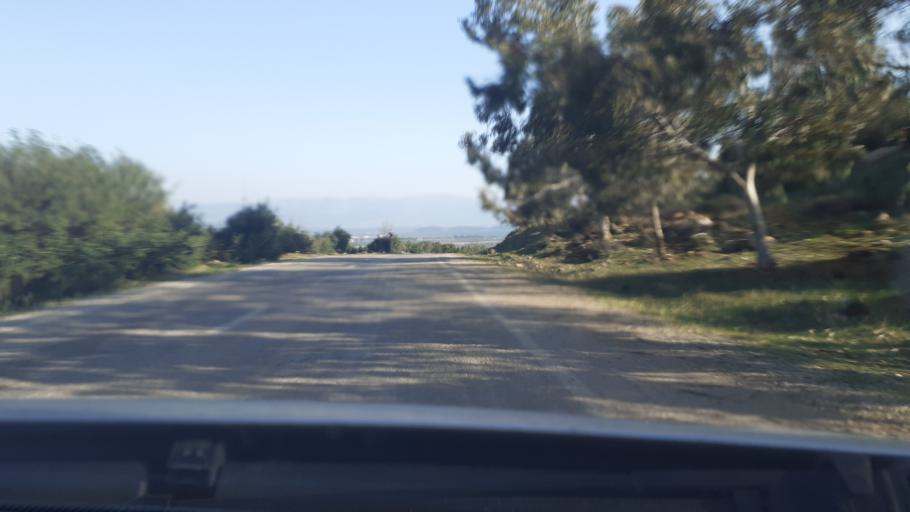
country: TR
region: Hatay
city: Aktepe
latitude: 36.7297
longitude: 36.4816
